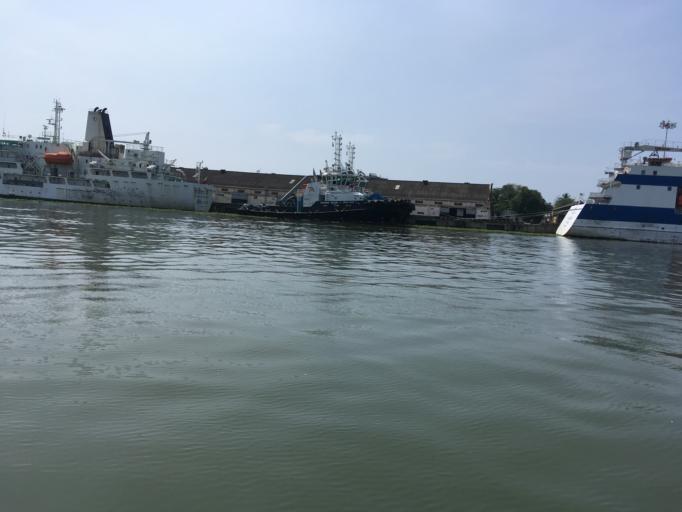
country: IN
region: Kerala
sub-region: Ernakulam
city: Cochin
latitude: 9.9697
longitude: 76.2661
